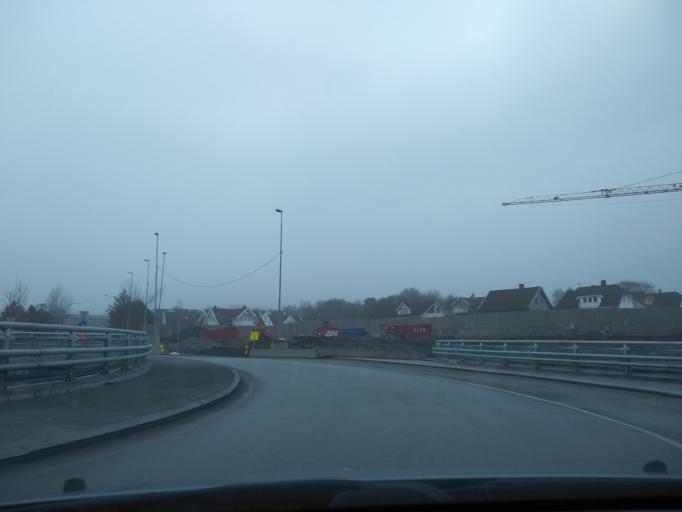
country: NO
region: Rogaland
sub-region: Stavanger
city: Stavanger
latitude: 58.9783
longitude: 5.6866
